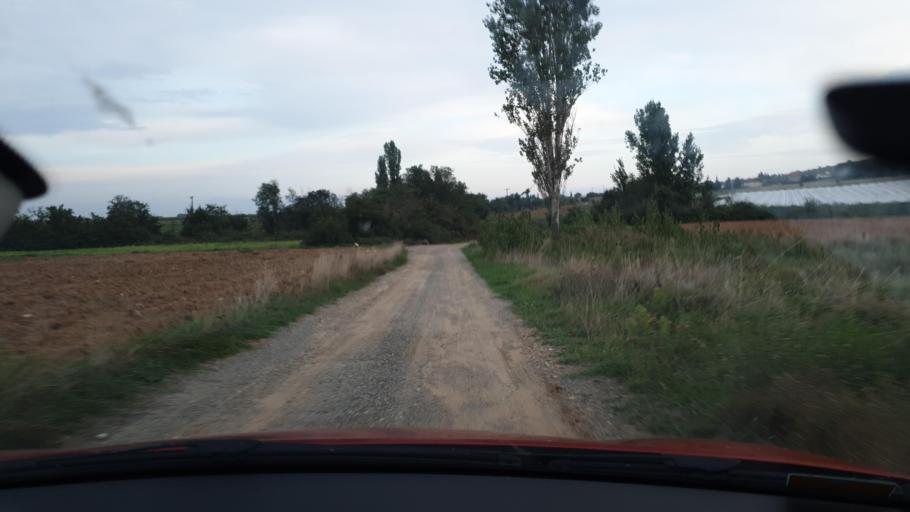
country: GR
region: Central Macedonia
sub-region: Nomos Kilkis
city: Kristoni
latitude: 40.9599
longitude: 22.8188
